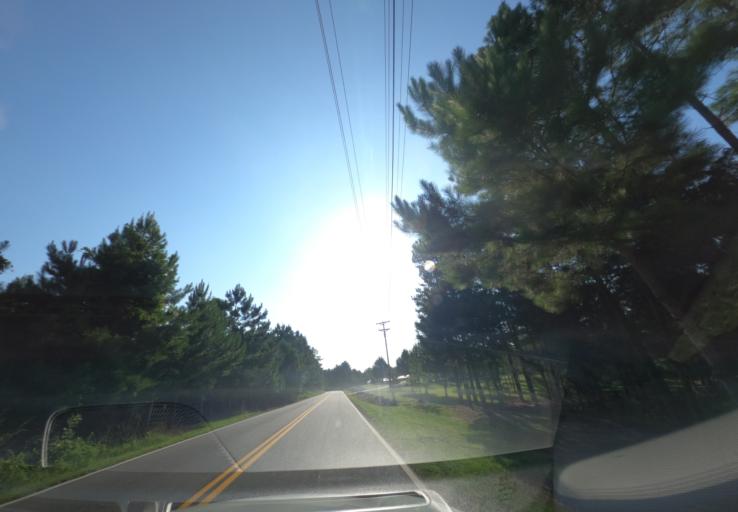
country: US
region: South Carolina
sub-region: Edgefield County
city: Murphys Estates
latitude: 33.5722
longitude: -82.0038
